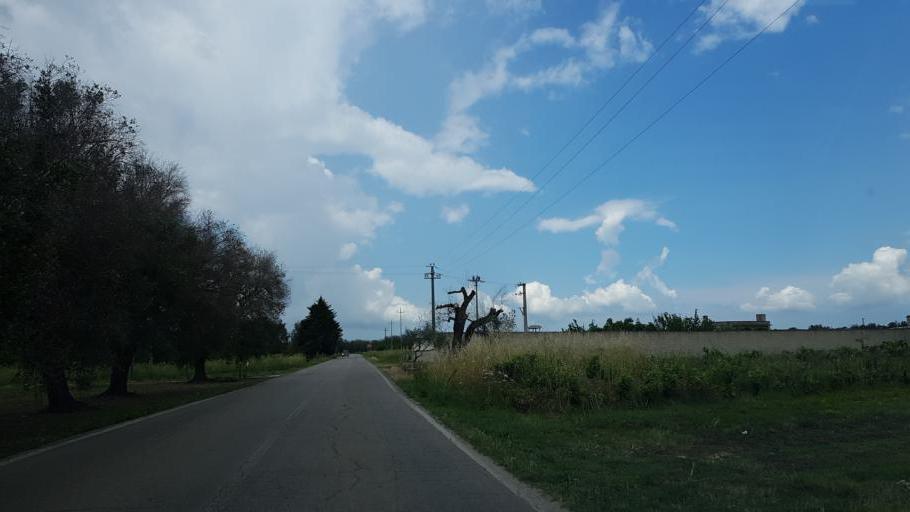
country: IT
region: Apulia
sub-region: Provincia di Brindisi
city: San Donaci
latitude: 40.4595
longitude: 17.9245
